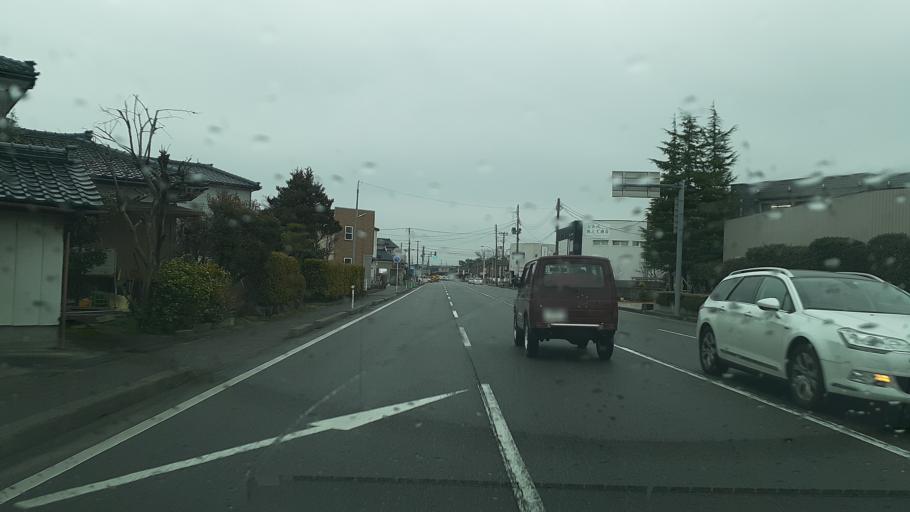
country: JP
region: Niigata
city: Kameda-honcho
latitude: 37.8760
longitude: 139.1140
